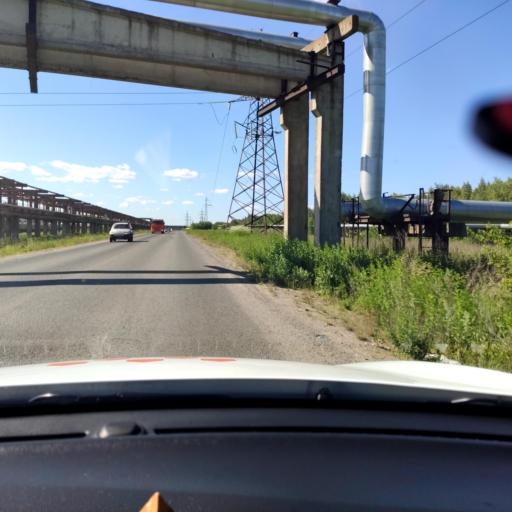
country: RU
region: Tatarstan
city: Staroye Arakchino
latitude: 55.8768
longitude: 48.9756
